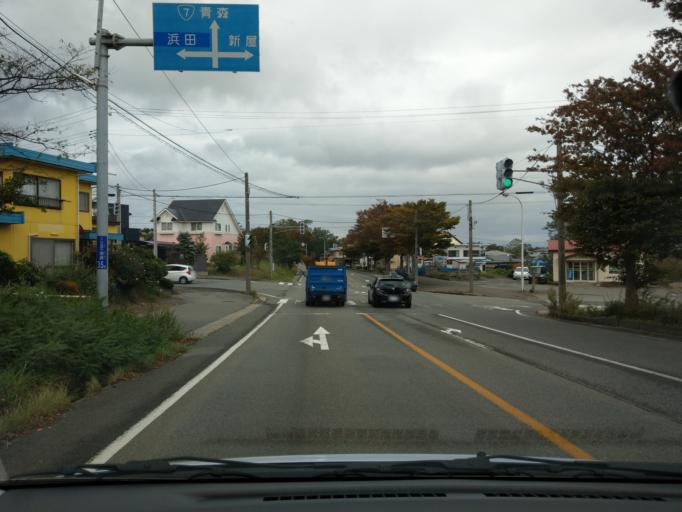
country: JP
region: Akita
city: Akita Shi
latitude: 39.6768
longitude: 140.0784
